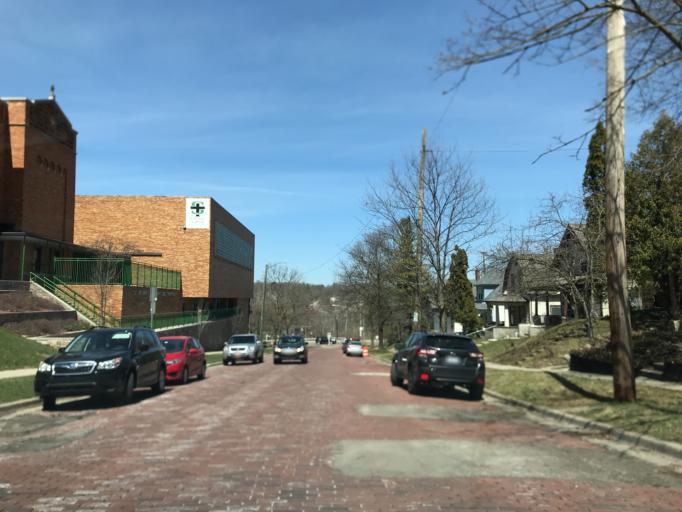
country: US
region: Michigan
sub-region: Washtenaw County
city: Ann Arbor
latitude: 42.2854
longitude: -83.7410
